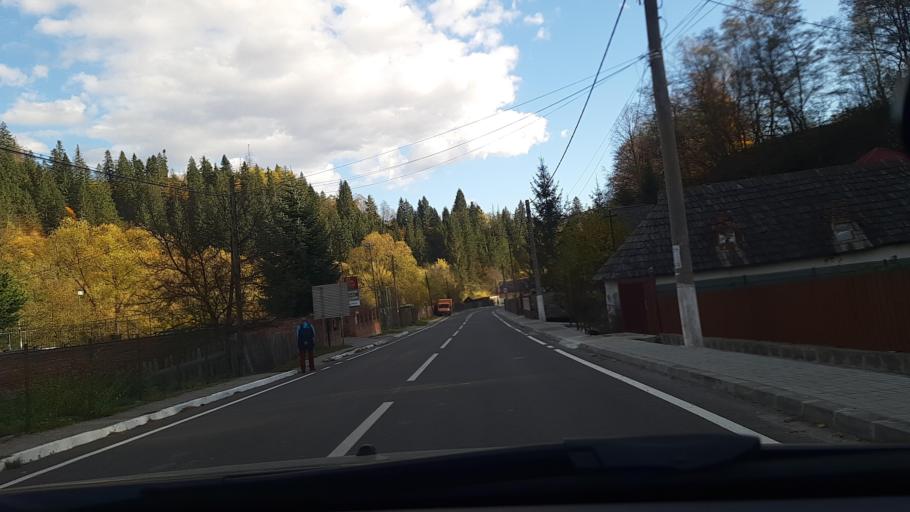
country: RO
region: Valcea
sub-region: Comuna Voineasa
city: Voineasa
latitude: 45.4249
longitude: 23.9505
